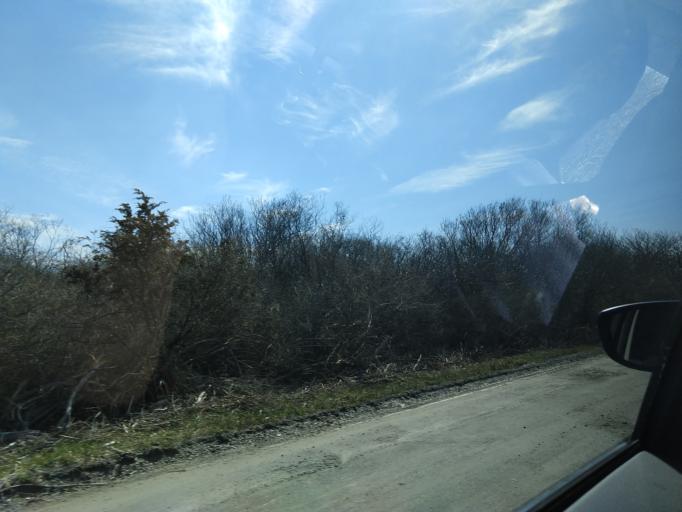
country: US
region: Massachusetts
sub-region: Essex County
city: Ipswich
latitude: 42.7185
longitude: -70.7809
